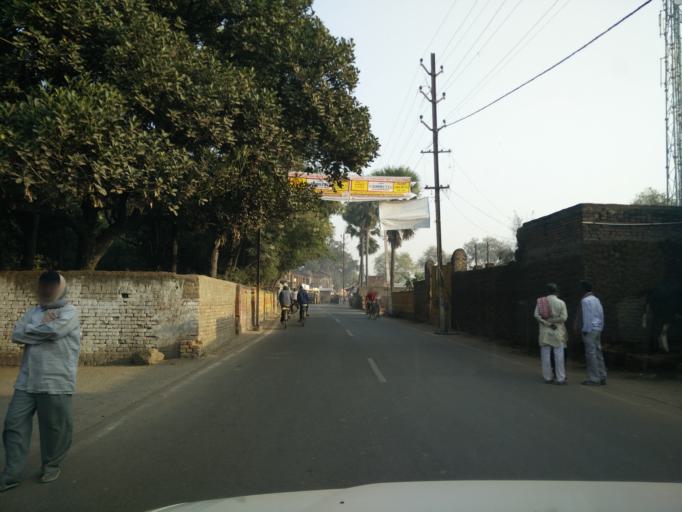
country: IN
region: Bihar
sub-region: Gaya
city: Gaya
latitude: 24.8106
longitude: 85.0153
